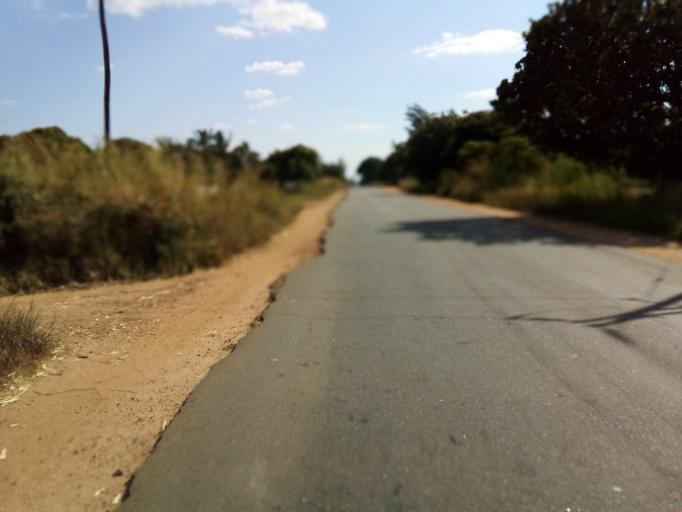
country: MZ
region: Zambezia
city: Quelimane
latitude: -17.5769
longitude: 36.6580
